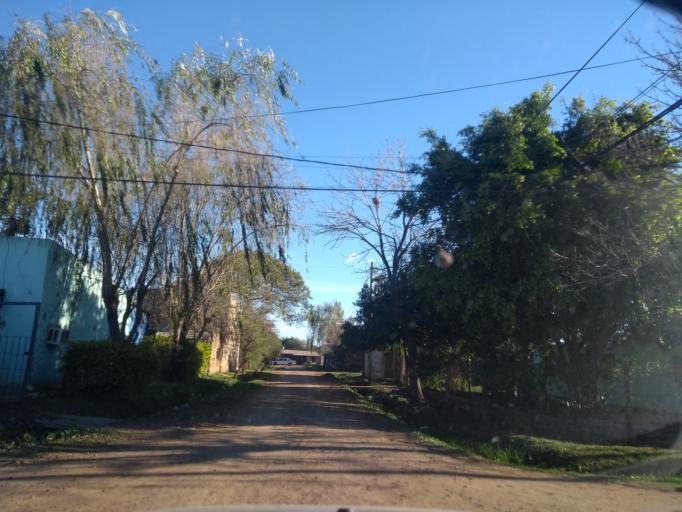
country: AR
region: Chaco
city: Barranqueras
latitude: -27.4738
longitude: -58.9289
